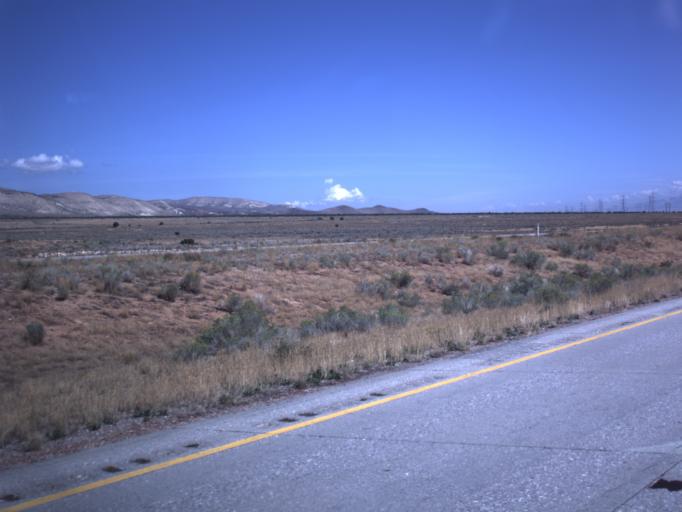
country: US
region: Utah
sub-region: Sevier County
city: Aurora
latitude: 38.8527
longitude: -111.9981
